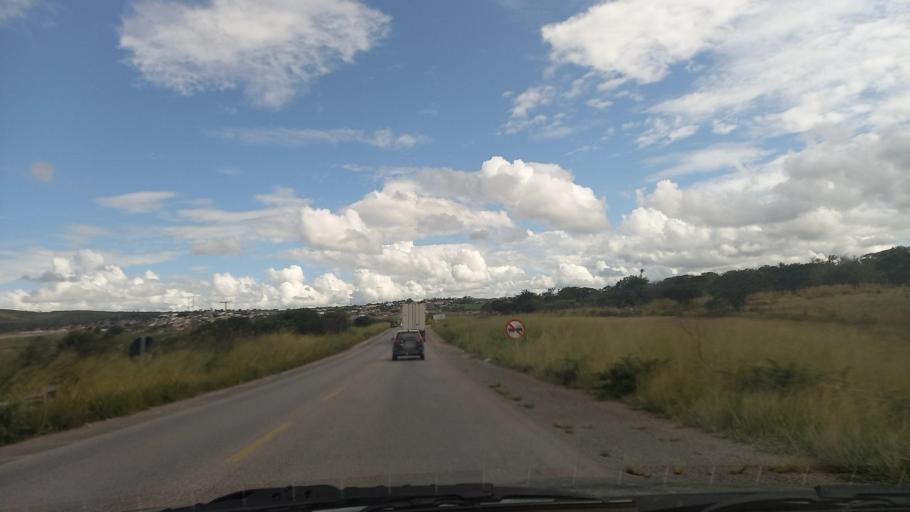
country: BR
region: Pernambuco
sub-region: Lajedo
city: Lajedo
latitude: -8.6933
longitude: -36.4120
